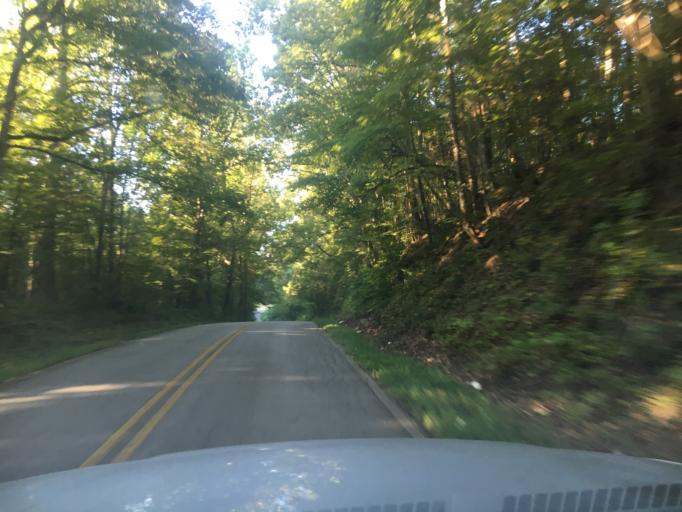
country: US
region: South Carolina
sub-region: Spartanburg County
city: Woodruff
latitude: 34.6702
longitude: -81.9636
